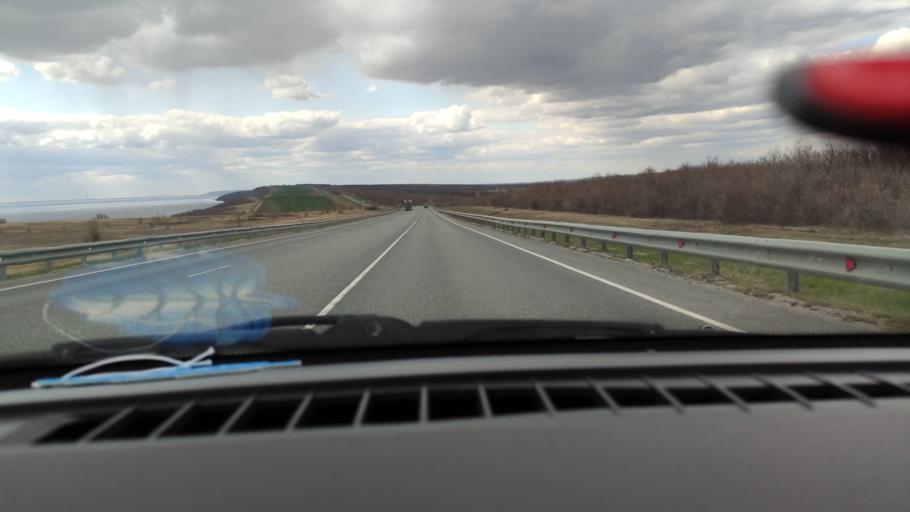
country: RU
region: Saratov
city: Balakovo
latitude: 52.2010
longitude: 47.8649
